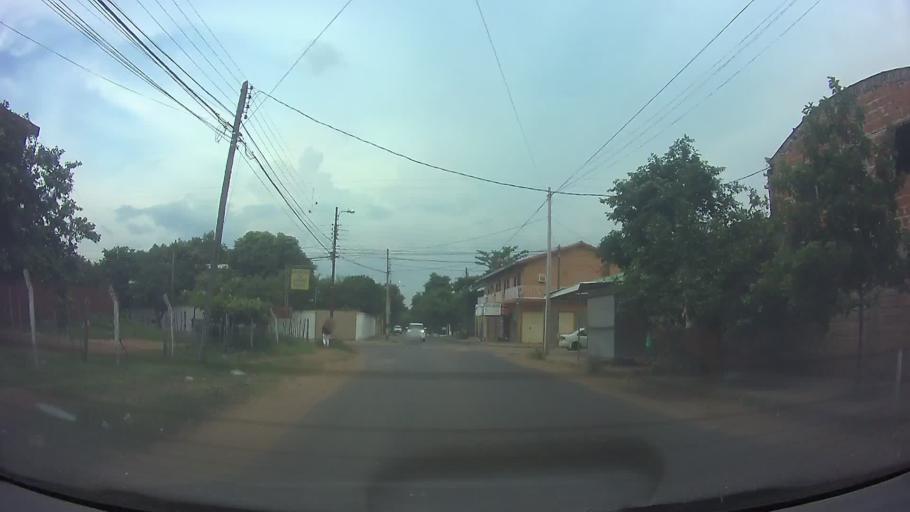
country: PY
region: Central
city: San Lorenzo
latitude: -25.2757
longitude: -57.4909
